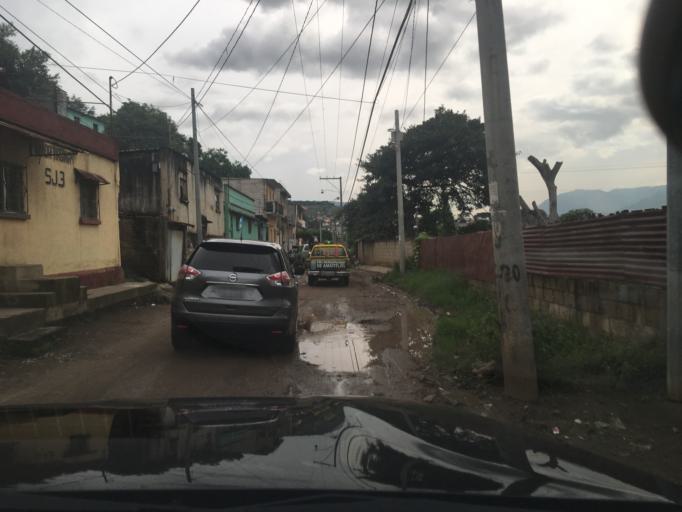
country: GT
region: Guatemala
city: Amatitlan
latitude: 14.4754
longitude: -90.6178
